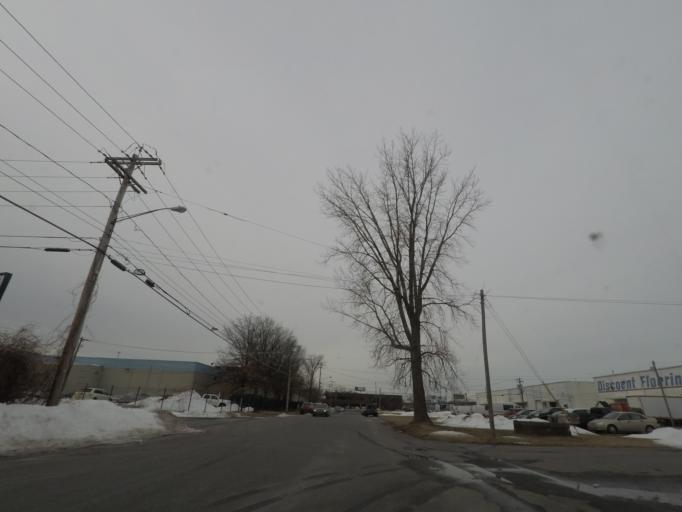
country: US
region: New York
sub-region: Albany County
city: West Albany
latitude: 42.6790
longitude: -73.7777
